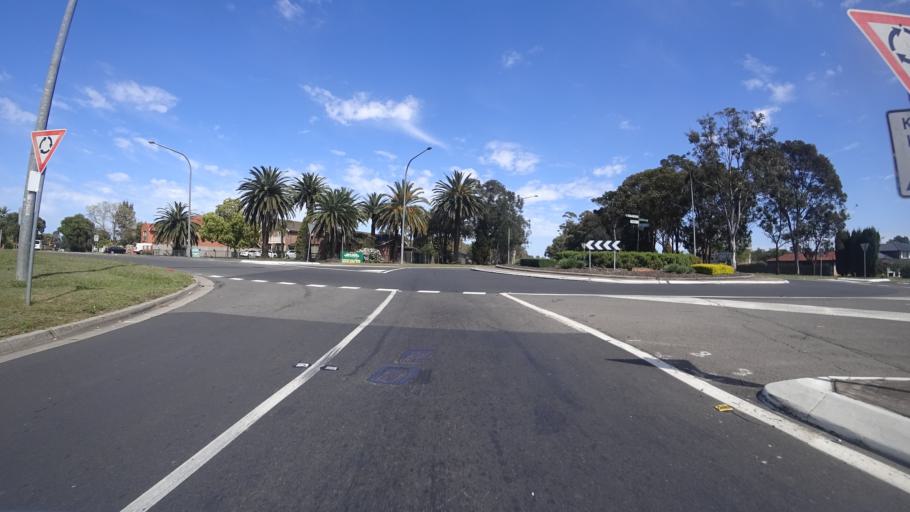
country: AU
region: New South Wales
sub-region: Fairfield
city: Chipping Norton
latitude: -33.9154
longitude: 150.9547
